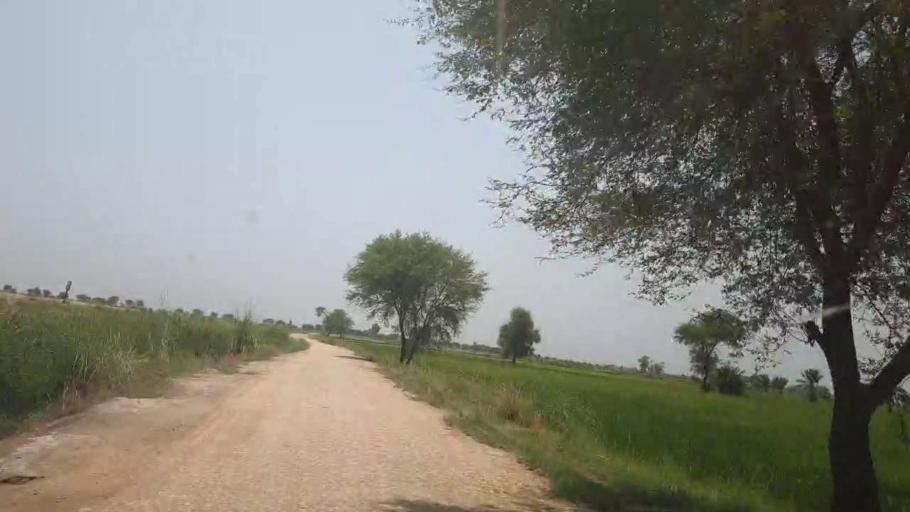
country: PK
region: Sindh
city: Lakhi
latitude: 27.8564
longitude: 68.6649
